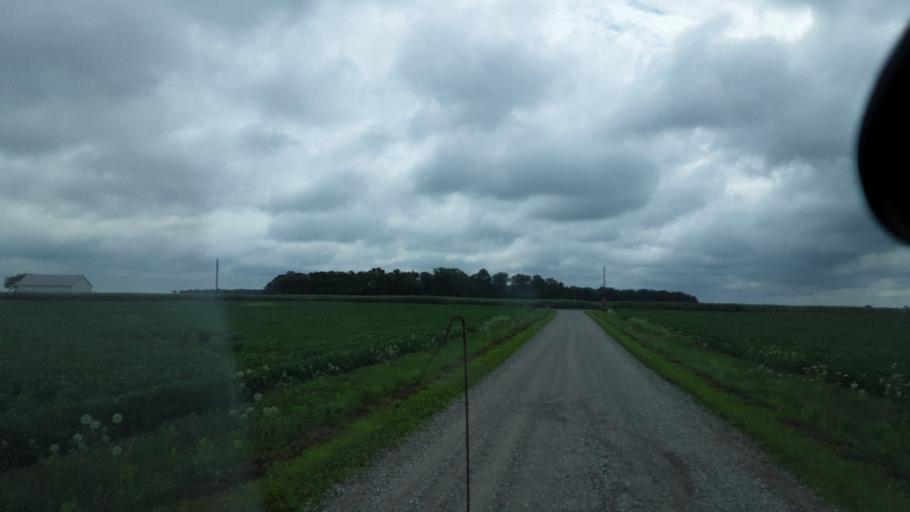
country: US
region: Indiana
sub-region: Wells County
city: Ossian
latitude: 40.8381
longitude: -85.0744
